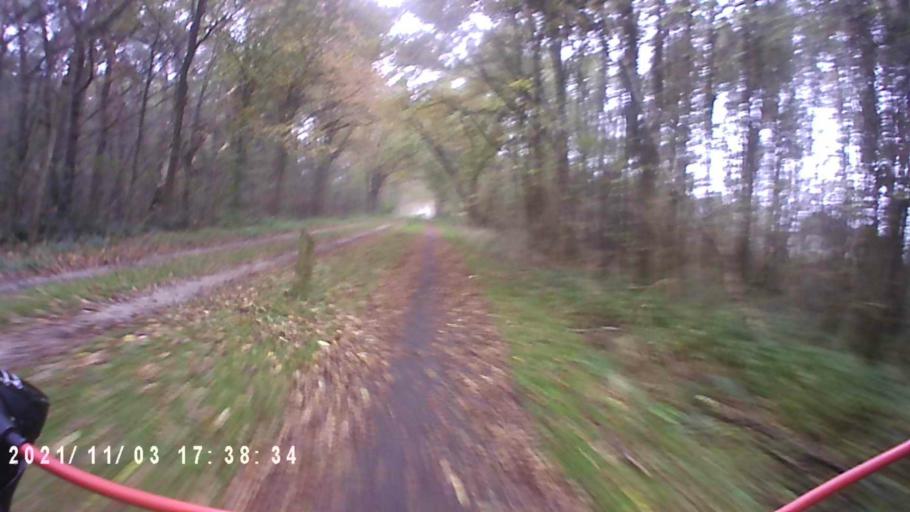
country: NL
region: Drenthe
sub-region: Gemeente Westerveld
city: Dwingeloo
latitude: 52.8695
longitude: 6.2904
